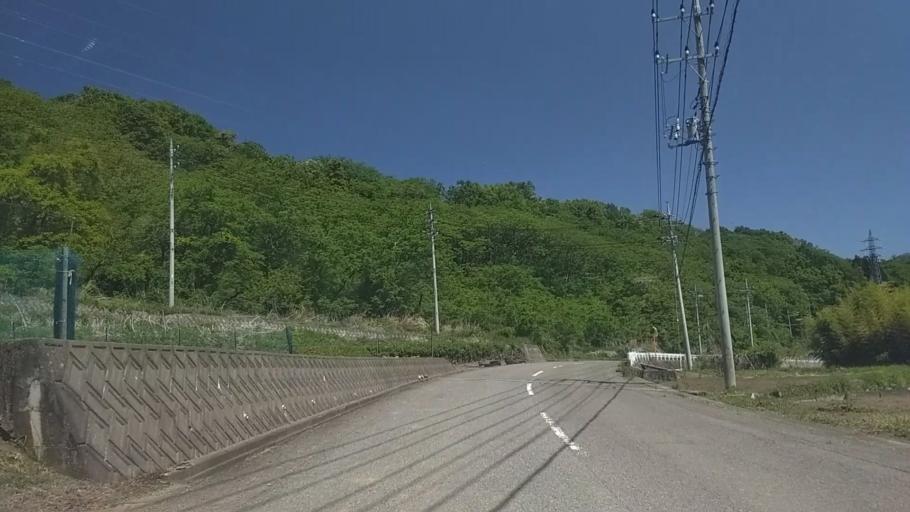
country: JP
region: Yamanashi
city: Nirasaki
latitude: 35.8548
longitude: 138.4345
